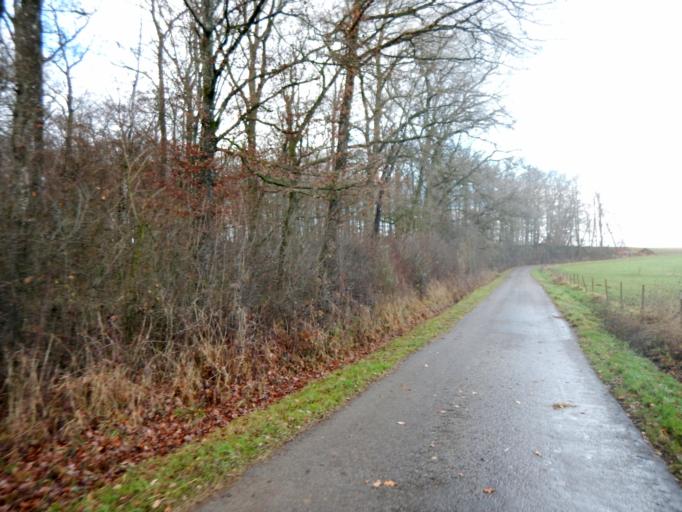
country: LU
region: Diekirch
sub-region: Canton de Redange
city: Redange-sur-Attert
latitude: 49.7586
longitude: 5.9108
